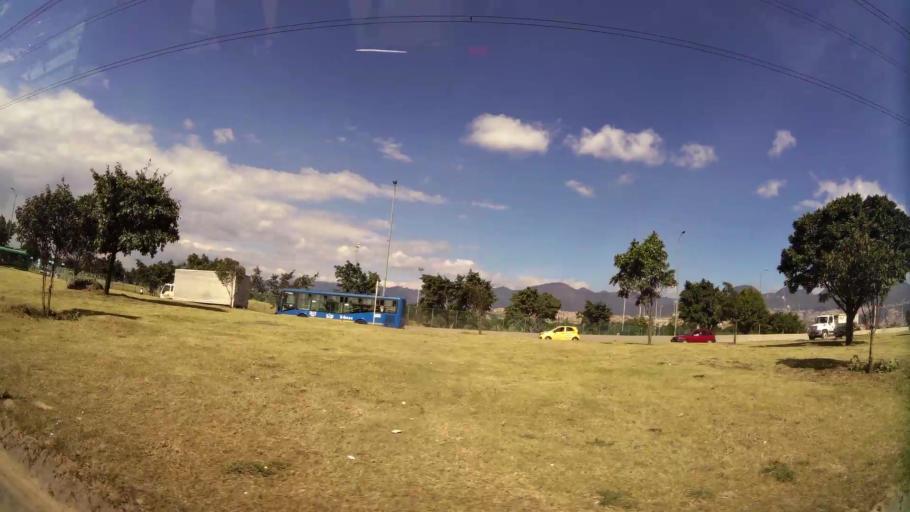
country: CO
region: Bogota D.C.
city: Bogota
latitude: 4.5692
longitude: -74.1387
